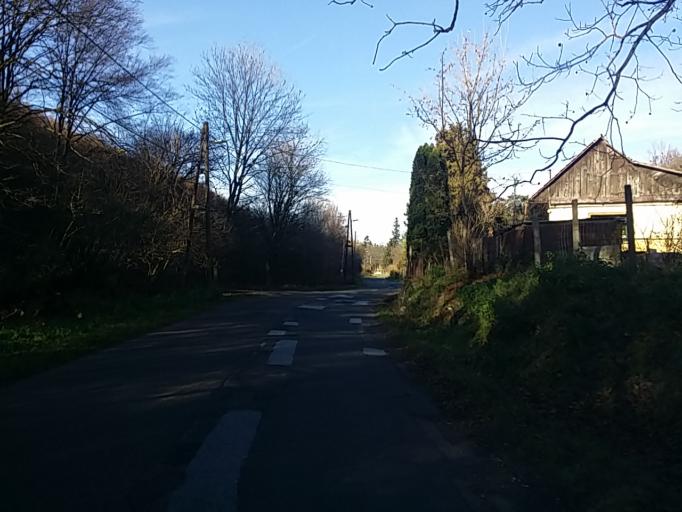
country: HU
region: Heves
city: Abasar
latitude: 47.8189
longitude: 19.9814
